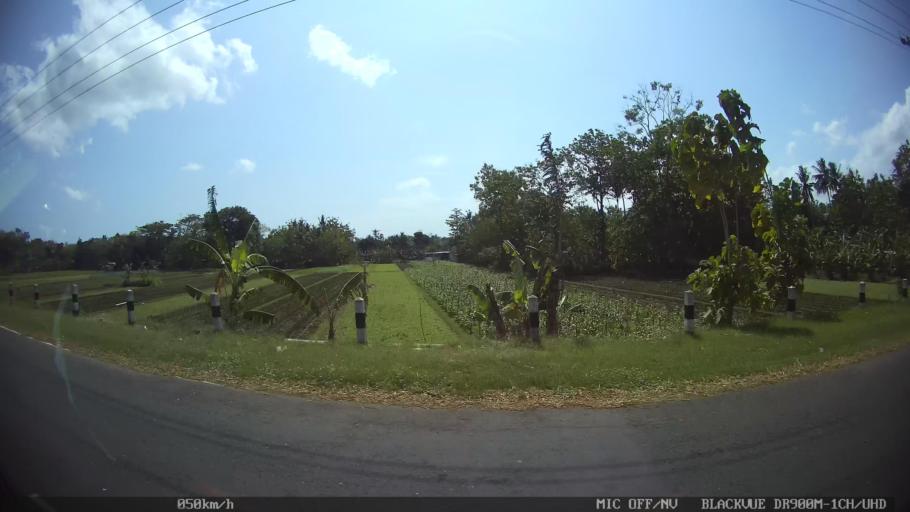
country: ID
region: Daerah Istimewa Yogyakarta
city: Pundong
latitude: -7.9608
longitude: 110.3570
